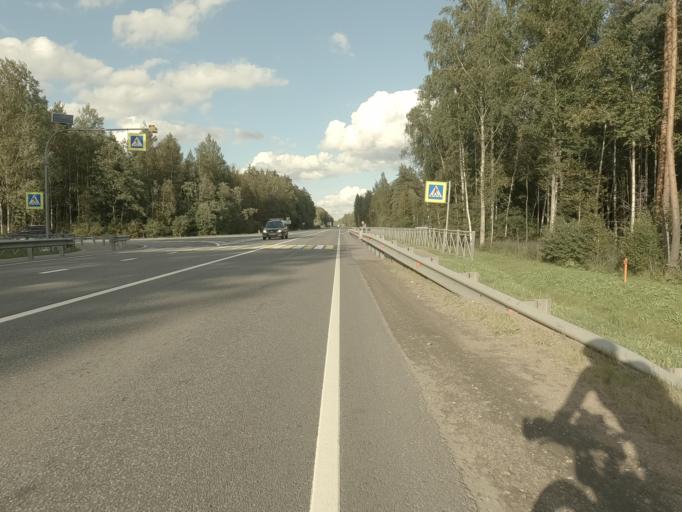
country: RU
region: Leningrad
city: Mga
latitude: 59.7070
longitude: 31.0149
